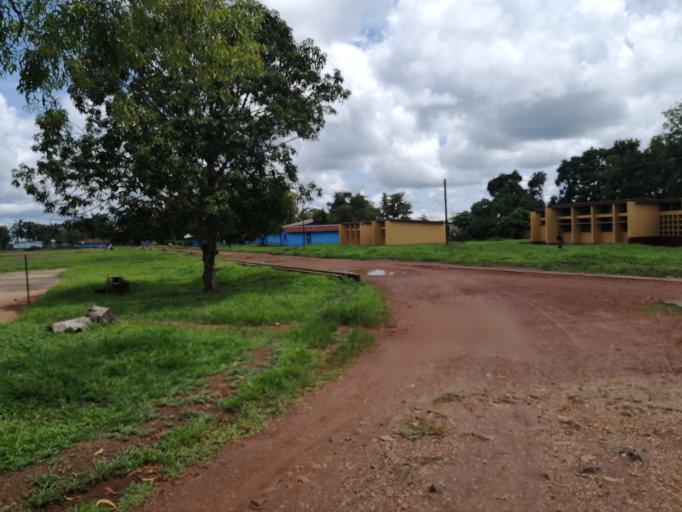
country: SL
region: Northern Province
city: Port Loko
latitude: 8.7768
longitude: -12.7902
